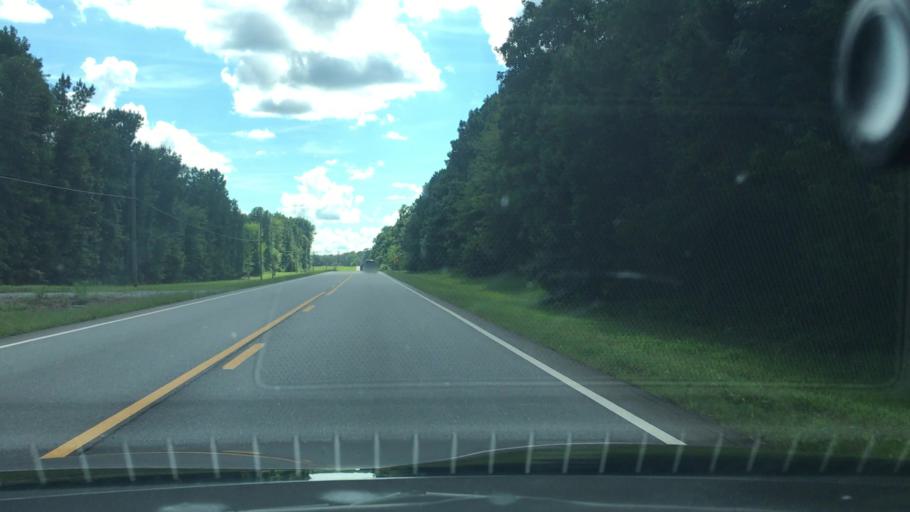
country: US
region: Georgia
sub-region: Butts County
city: Jackson
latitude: 33.2864
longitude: -84.0295
